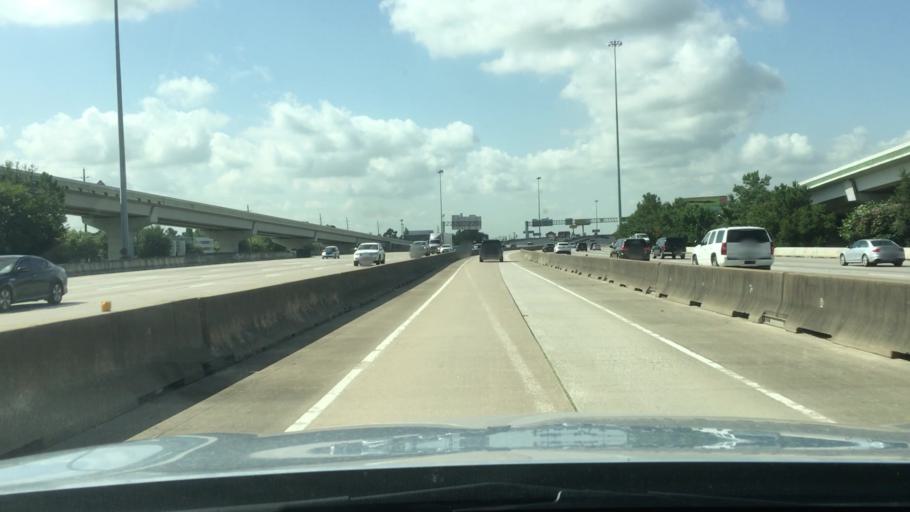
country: US
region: Texas
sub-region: Harris County
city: Aldine
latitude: 29.9373
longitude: -95.4128
